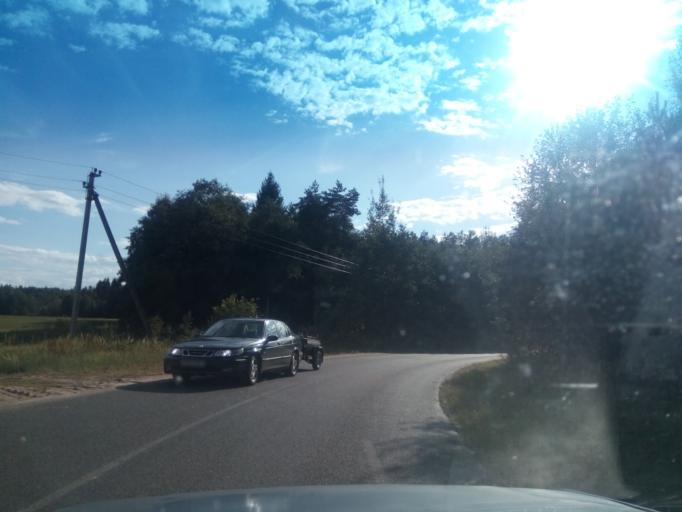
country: BY
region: Vitebsk
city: Polatsk
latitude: 55.4281
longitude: 28.7671
